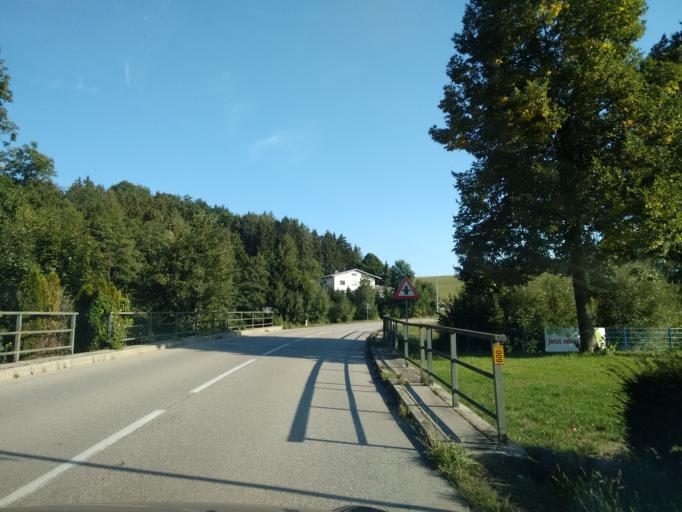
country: AT
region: Upper Austria
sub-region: Wels-Land
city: Marchtrenk
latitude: 48.1500
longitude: 14.1794
